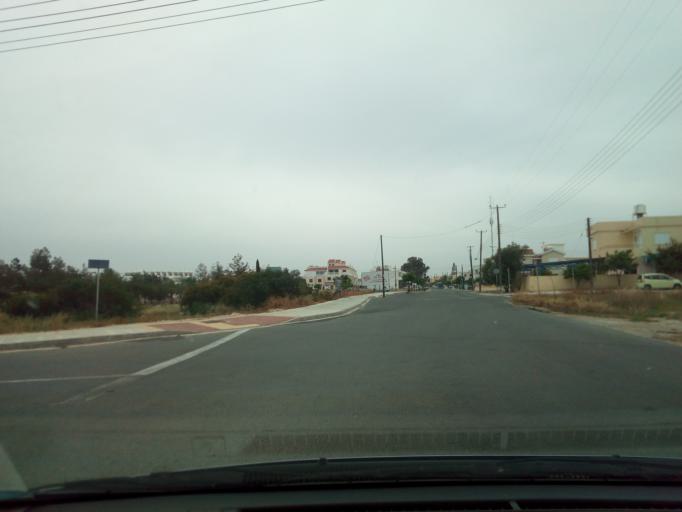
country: CY
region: Ammochostos
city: Paralimni
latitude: 35.0539
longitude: 33.9840
